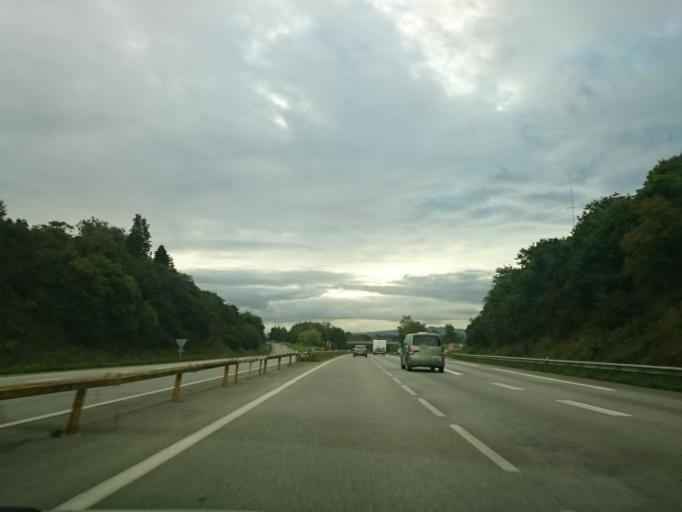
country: FR
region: Brittany
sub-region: Departement du Finistere
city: Chateaulin
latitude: 48.2167
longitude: -4.0557
